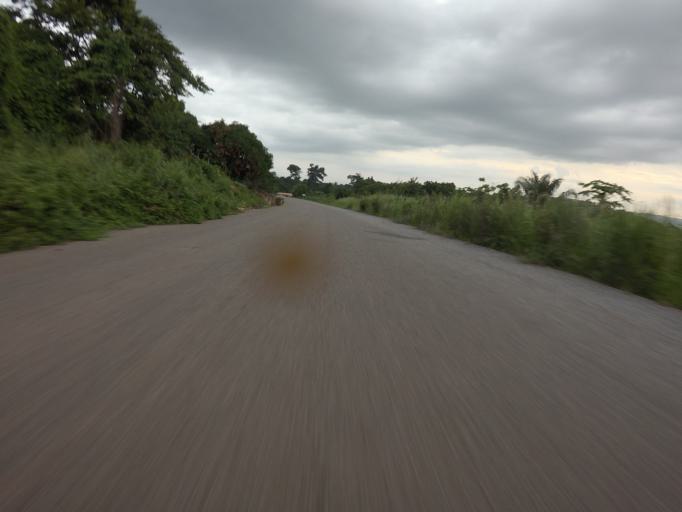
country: GH
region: Volta
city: Ho
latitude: 6.7866
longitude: 0.3668
